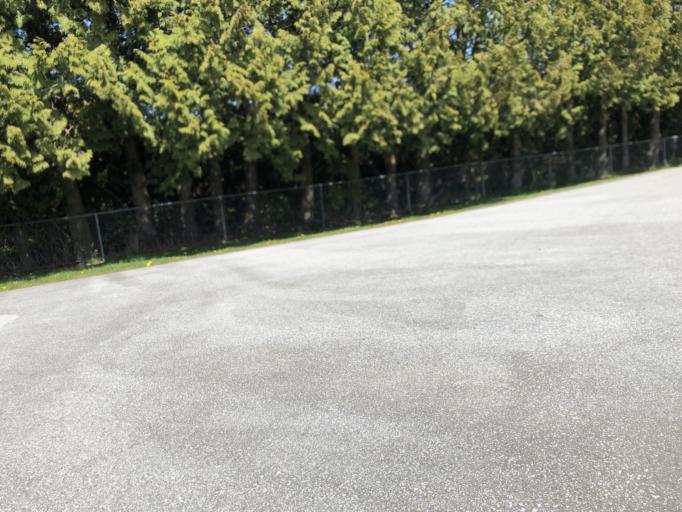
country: CA
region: British Columbia
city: Richmond
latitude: 49.1509
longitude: -123.1192
